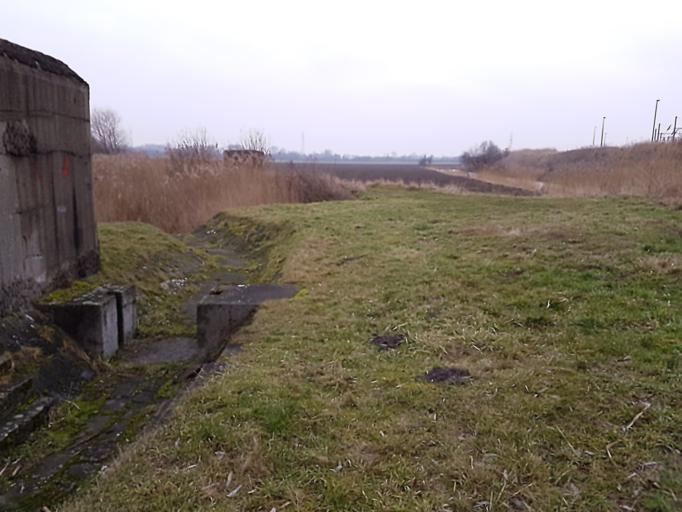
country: BE
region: Flanders
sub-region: Provincie Antwerpen
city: Stabroek
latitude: 51.3354
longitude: 4.3355
